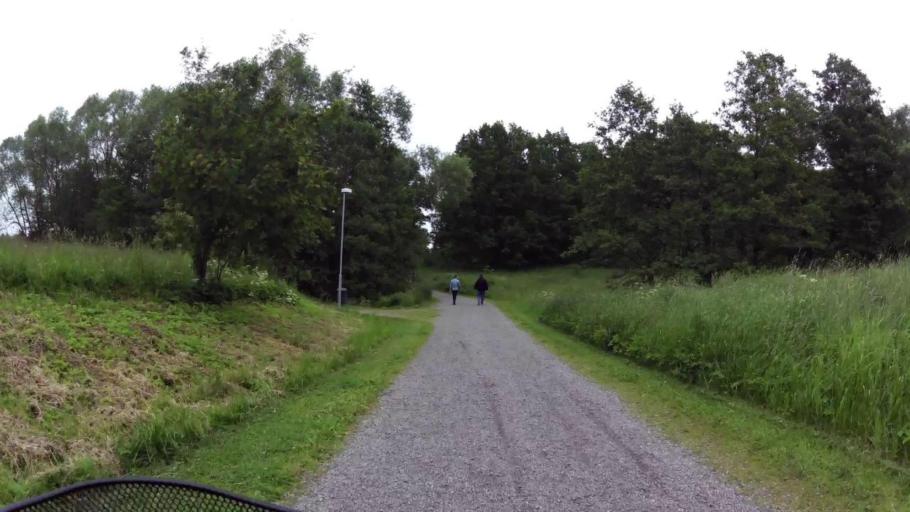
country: SE
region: OEstergoetland
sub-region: Linkopings Kommun
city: Linkoping
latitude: 58.3706
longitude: 15.6632
